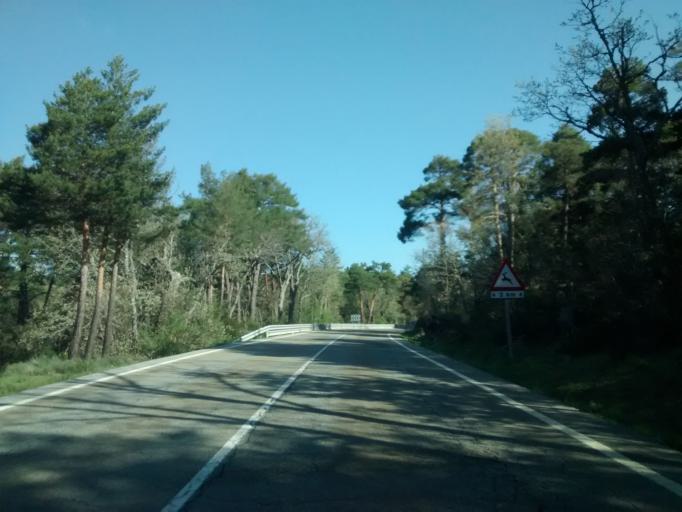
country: ES
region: Castille and Leon
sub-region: Provincia de Segovia
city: San Ildefonso
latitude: 40.8633
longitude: -4.0267
